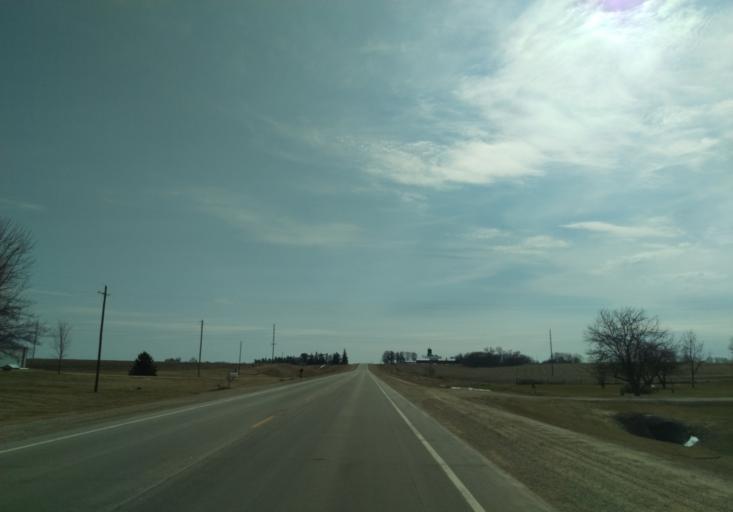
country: US
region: Minnesota
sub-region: Fillmore County
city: Harmony
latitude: 43.4816
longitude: -91.8704
